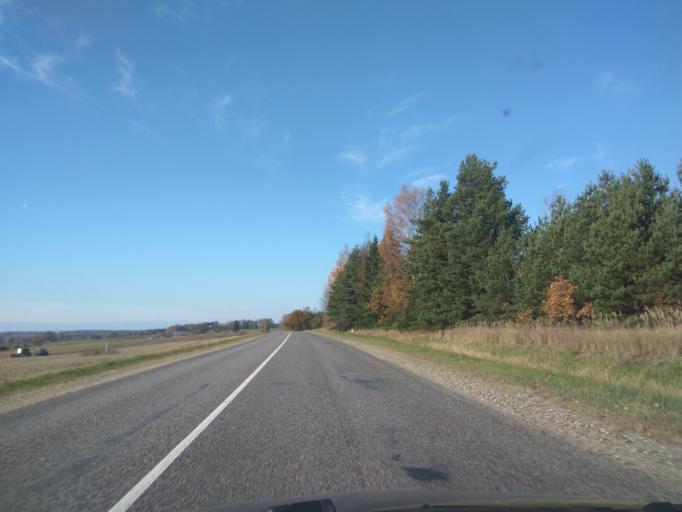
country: LV
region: Kuldigas Rajons
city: Kuldiga
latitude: 57.0269
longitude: 21.8572
